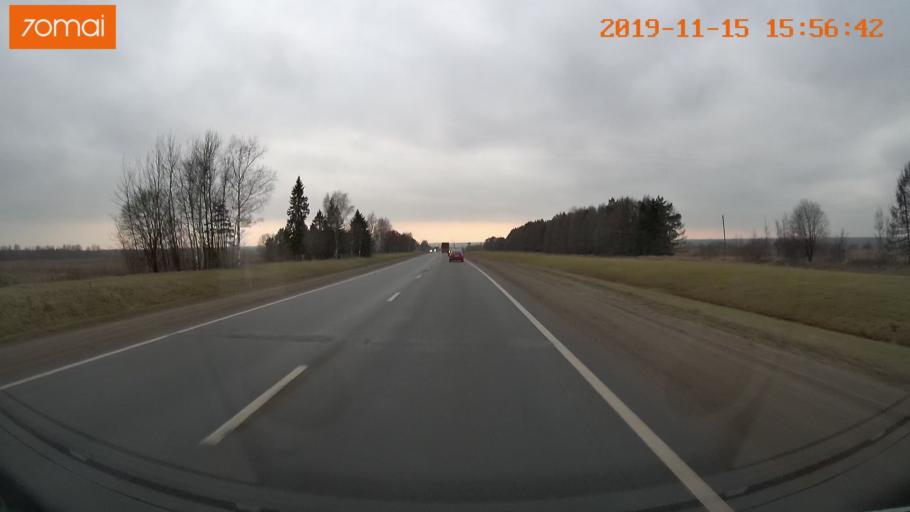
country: RU
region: Jaroslavl
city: Yaroslavl
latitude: 57.8390
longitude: 39.9706
